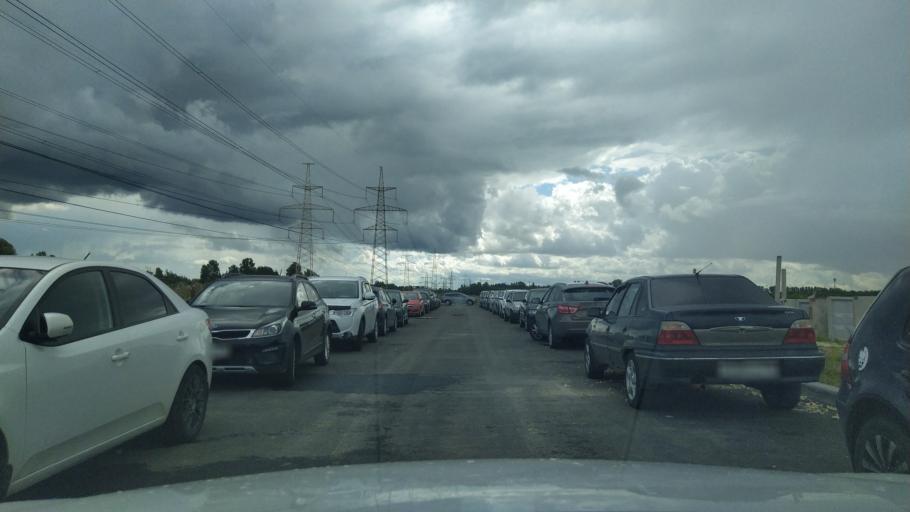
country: RU
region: St.-Petersburg
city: Krasnogvargeisky
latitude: 60.0018
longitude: 30.4834
